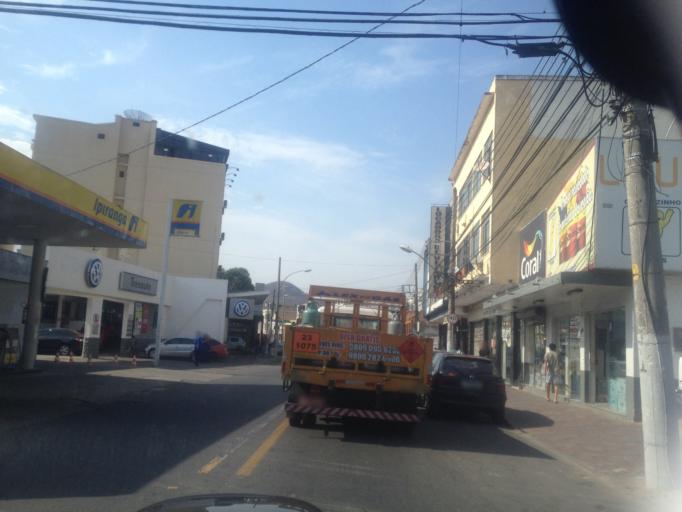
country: BR
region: Rio de Janeiro
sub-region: Tres Rios
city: Tres Rios
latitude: -22.1115
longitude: -43.2105
